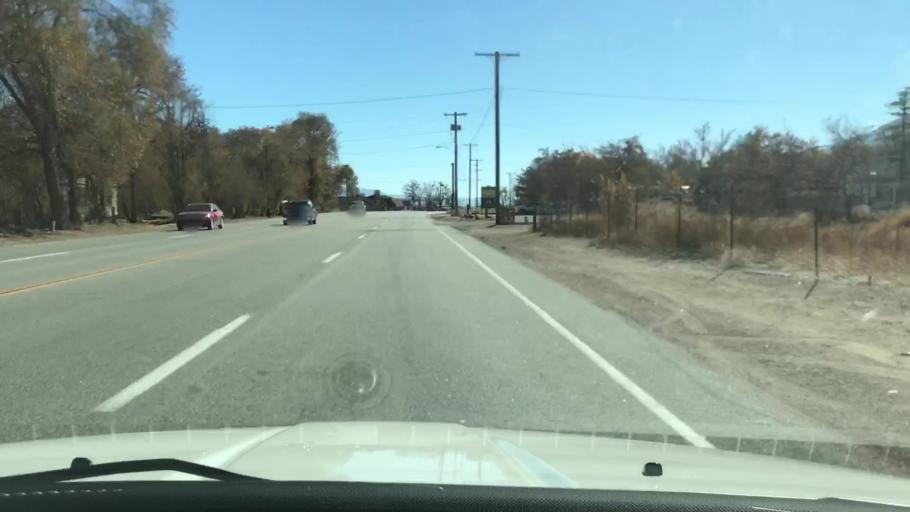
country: US
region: California
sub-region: Inyo County
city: Lone Pine
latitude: 36.5958
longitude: -118.0586
